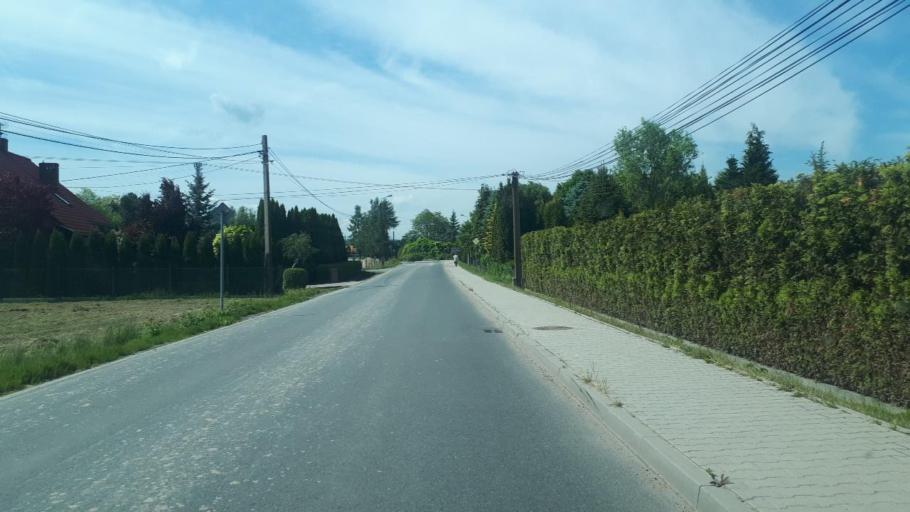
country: PL
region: Silesian Voivodeship
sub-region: Powiat bielski
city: Pisarzowice
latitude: 49.8822
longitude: 19.1447
